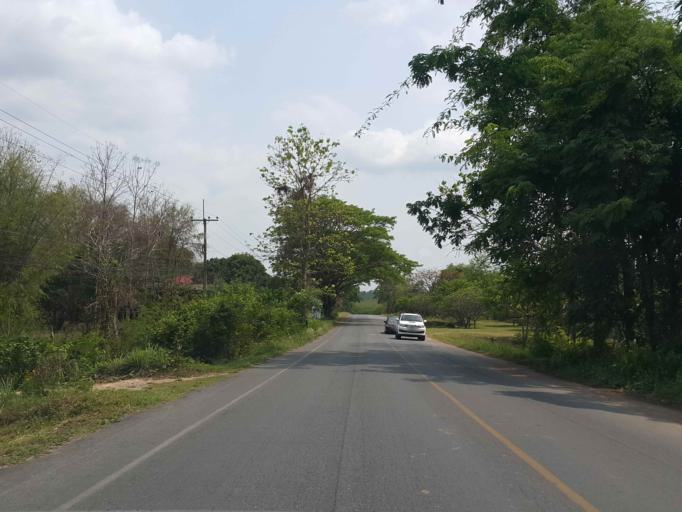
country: TH
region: Lampang
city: Thoen
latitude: 17.5743
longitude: 99.3293
